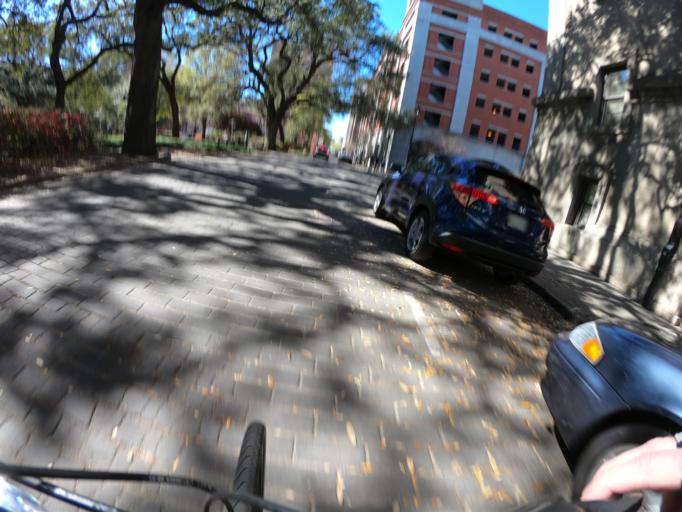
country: US
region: Georgia
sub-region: Chatham County
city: Savannah
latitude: 32.0796
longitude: -81.0889
